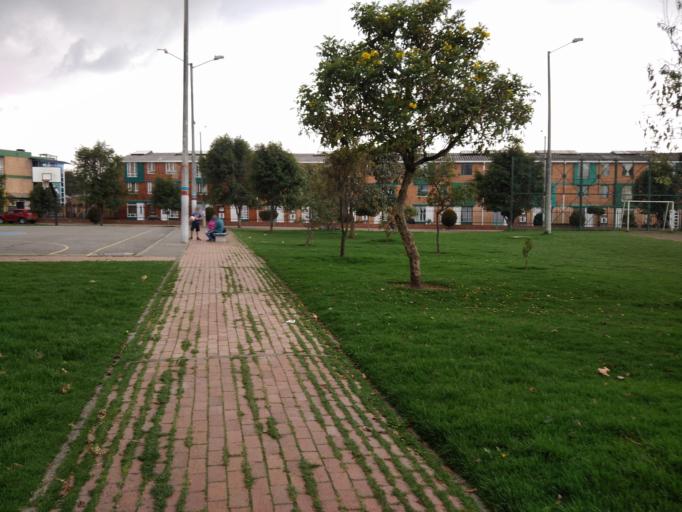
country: CO
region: Cundinamarca
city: Funza
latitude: 4.6714
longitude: -74.1570
